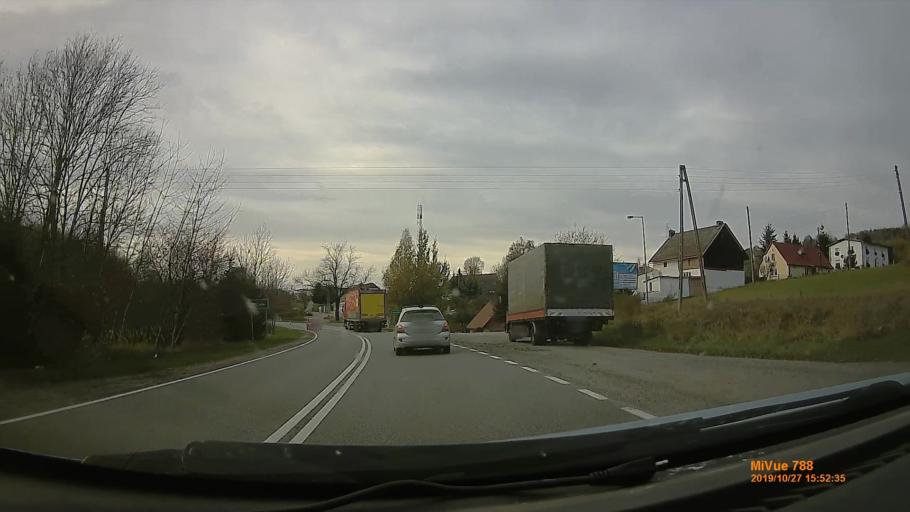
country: PL
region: Lower Silesian Voivodeship
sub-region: Powiat klodzki
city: Bozkow
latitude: 50.5358
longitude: 16.5782
